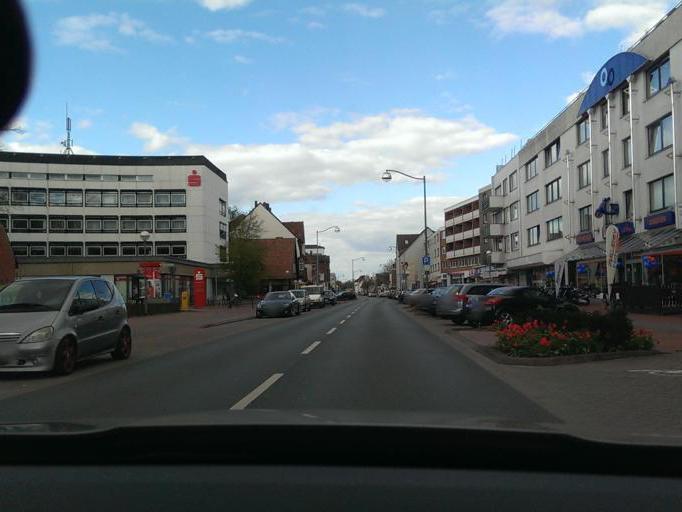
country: DE
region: Lower Saxony
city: Langenhagen
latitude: 52.4479
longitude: 9.7402
